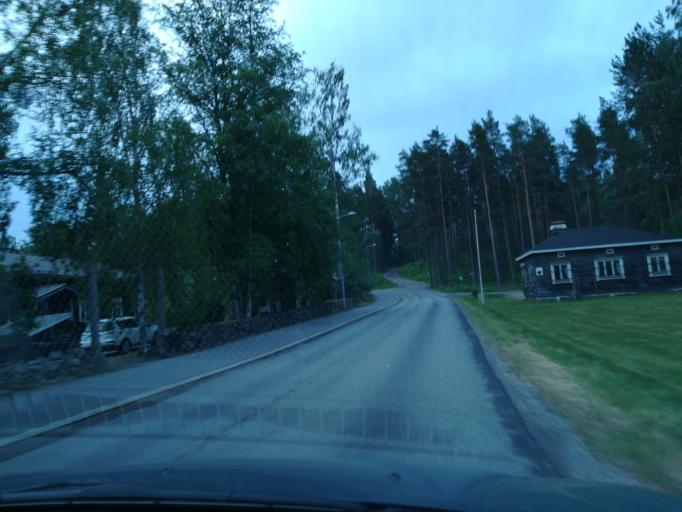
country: FI
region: Southern Savonia
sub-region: Mikkeli
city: Ristiina
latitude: 61.4986
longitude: 27.2700
